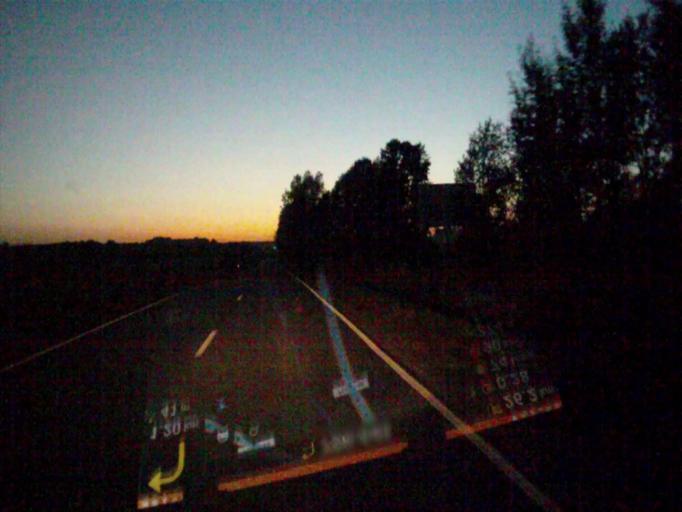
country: RU
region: Chelyabinsk
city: Chebarkul'
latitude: 55.2245
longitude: 60.4684
